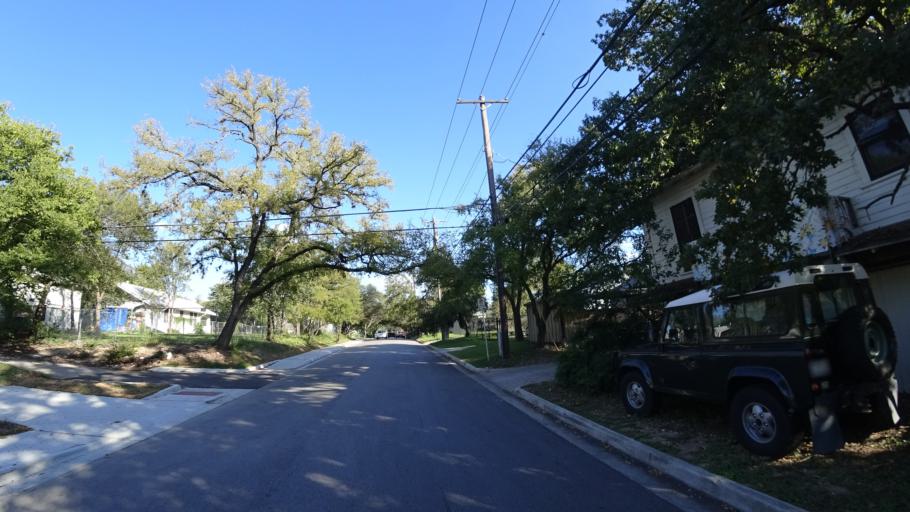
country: US
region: Texas
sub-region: Travis County
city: Austin
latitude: 30.2989
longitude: -97.7368
